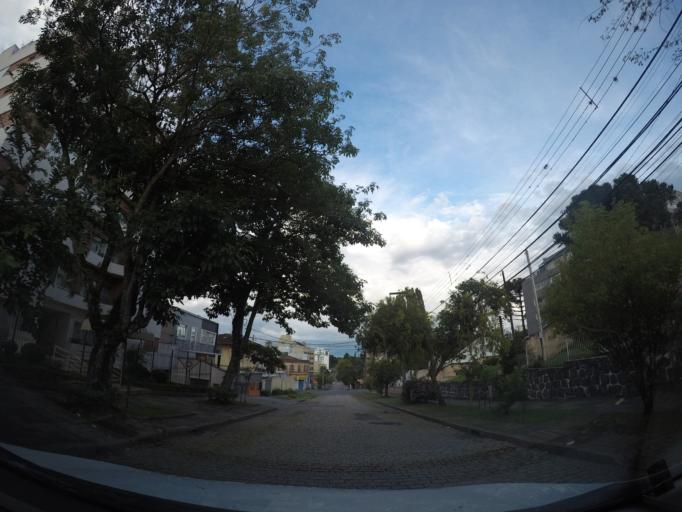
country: BR
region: Parana
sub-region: Curitiba
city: Curitiba
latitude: -25.4234
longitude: -49.2835
